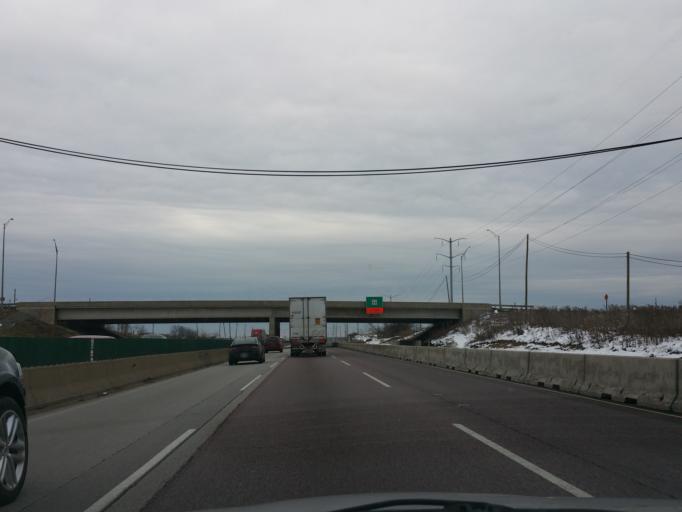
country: US
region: Illinois
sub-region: Kane County
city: East Dundee
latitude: 42.0663
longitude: -88.2252
